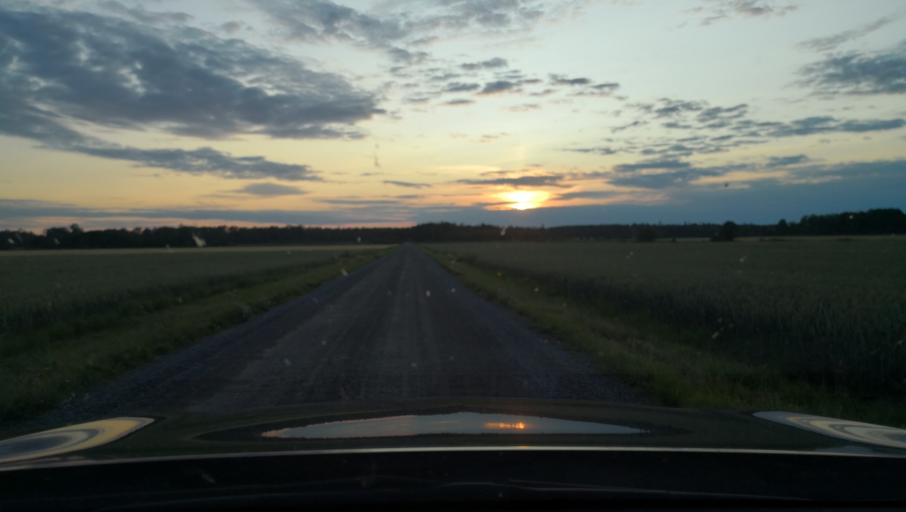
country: SE
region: Uppsala
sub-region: Osthammars Kommun
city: Bjorklinge
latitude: 60.0569
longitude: 17.5920
